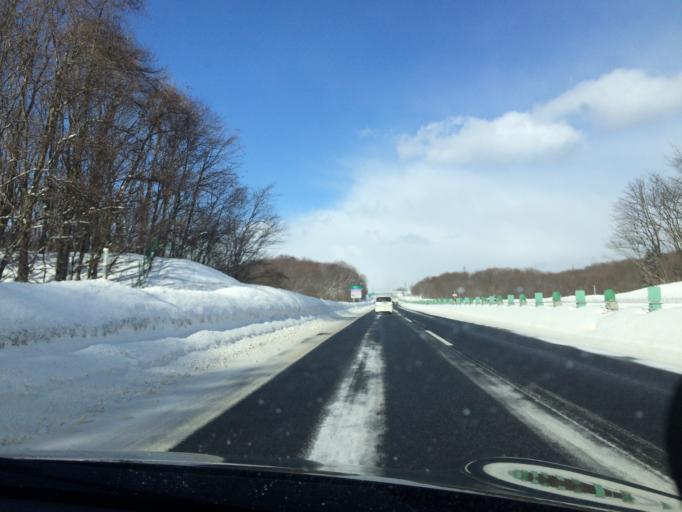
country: JP
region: Hokkaido
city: Kitahiroshima
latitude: 42.9418
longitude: 141.5202
